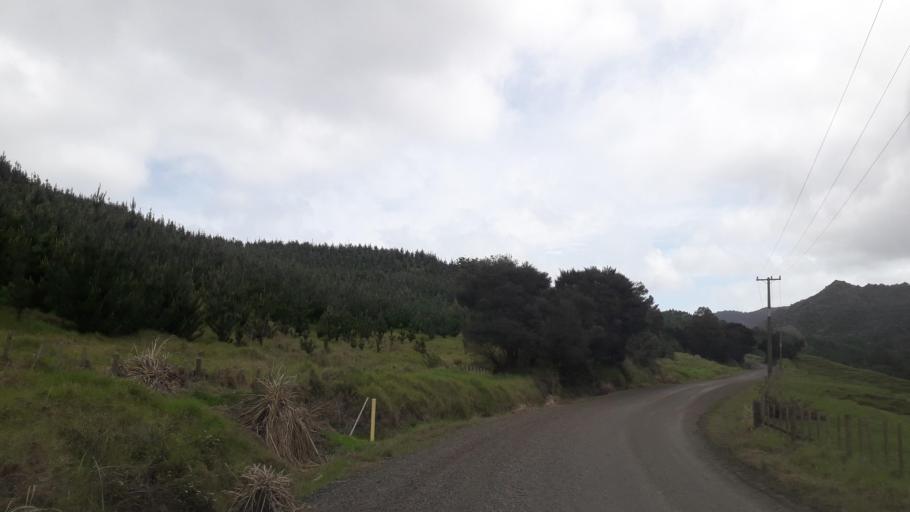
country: NZ
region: Northland
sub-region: Far North District
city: Ahipara
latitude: -35.4349
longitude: 173.3406
